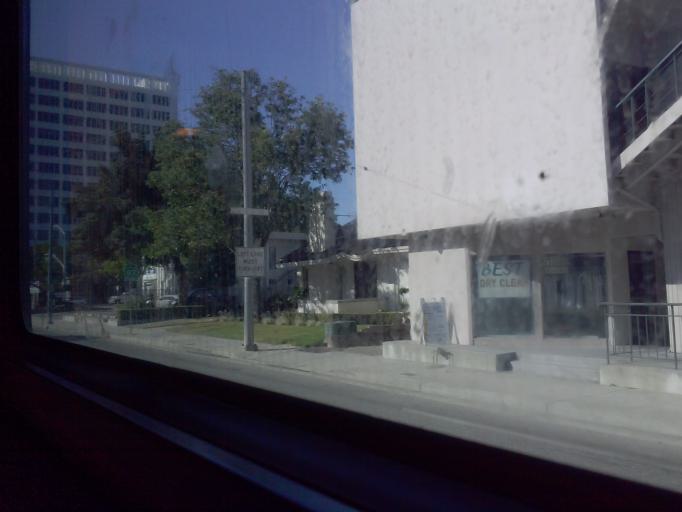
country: US
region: California
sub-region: Santa Clara County
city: San Jose
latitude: 37.3498
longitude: -121.9009
